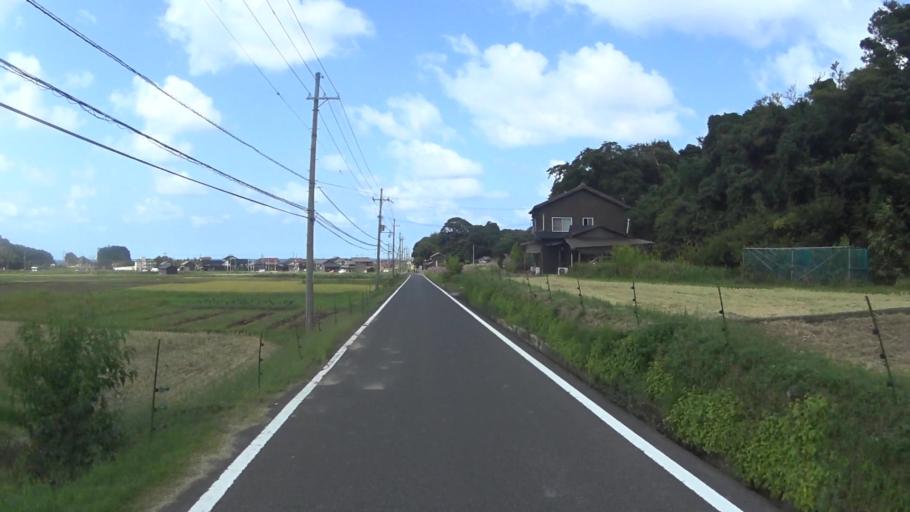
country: JP
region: Kyoto
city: Miyazu
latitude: 35.7532
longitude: 135.1759
